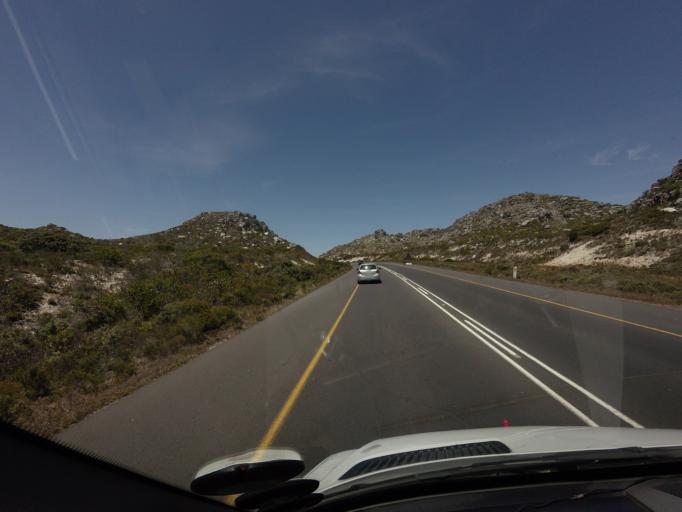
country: ZA
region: Western Cape
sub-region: City of Cape Town
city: Bergvliet
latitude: -34.1414
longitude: 18.3978
